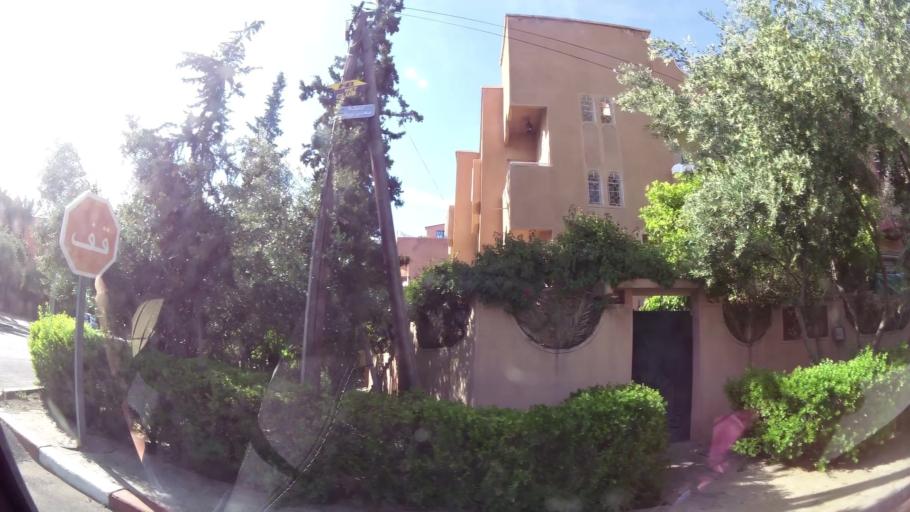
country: MA
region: Marrakech-Tensift-Al Haouz
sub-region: Marrakech
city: Marrakesh
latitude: 31.6528
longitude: -8.0077
